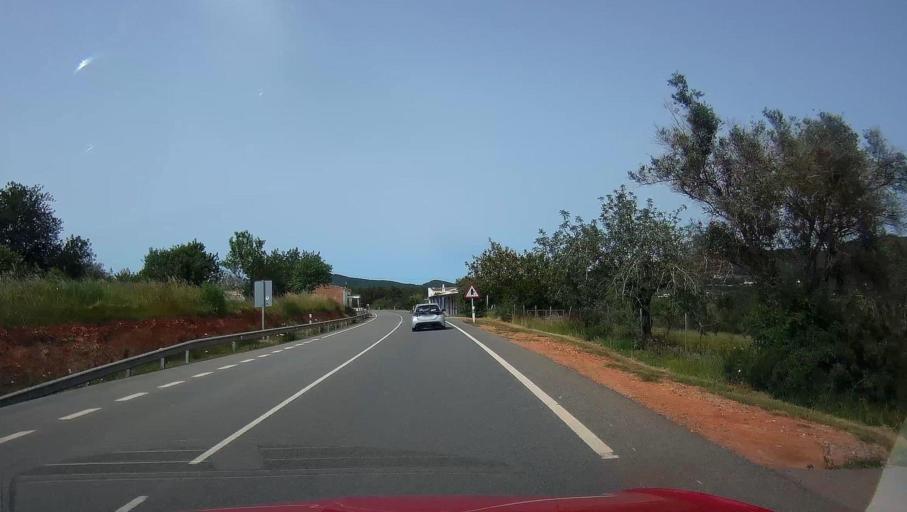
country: ES
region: Balearic Islands
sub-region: Illes Balears
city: Sant Joan de Labritja
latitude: 39.0395
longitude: 1.4921
